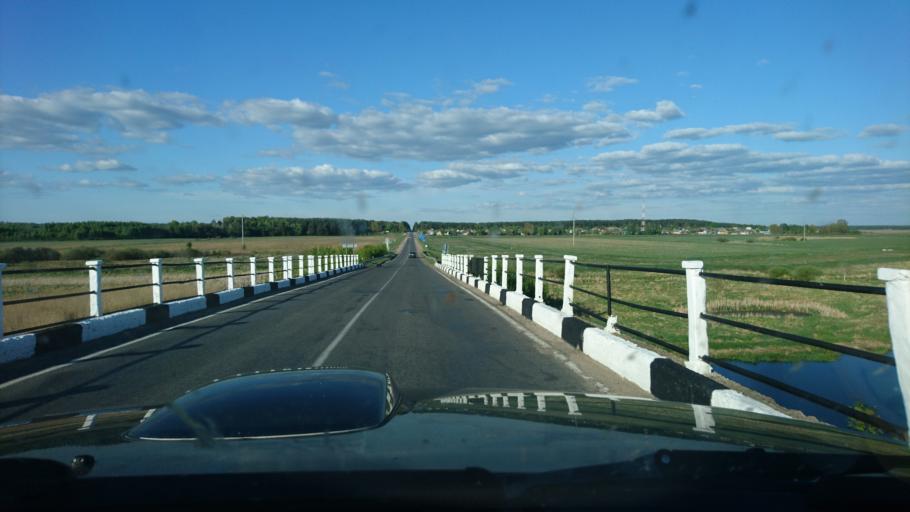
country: BY
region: Brest
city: Ivatsevichy
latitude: 52.7201
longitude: 25.3598
